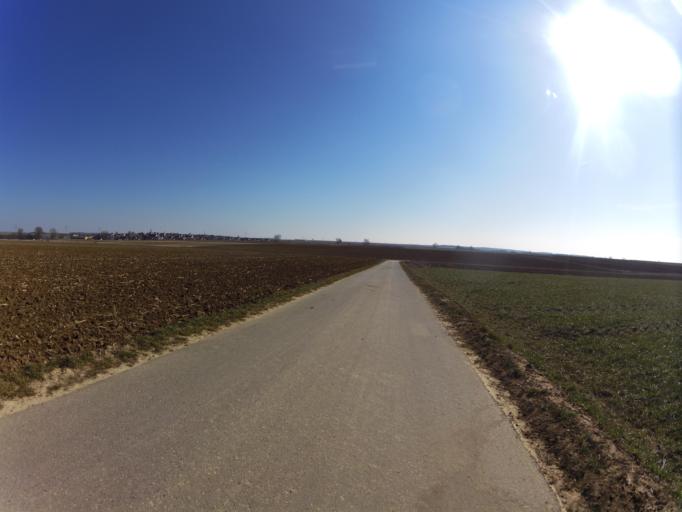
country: DE
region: Bavaria
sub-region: Regierungsbezirk Unterfranken
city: Bergtheim
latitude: 49.8861
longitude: 10.0716
